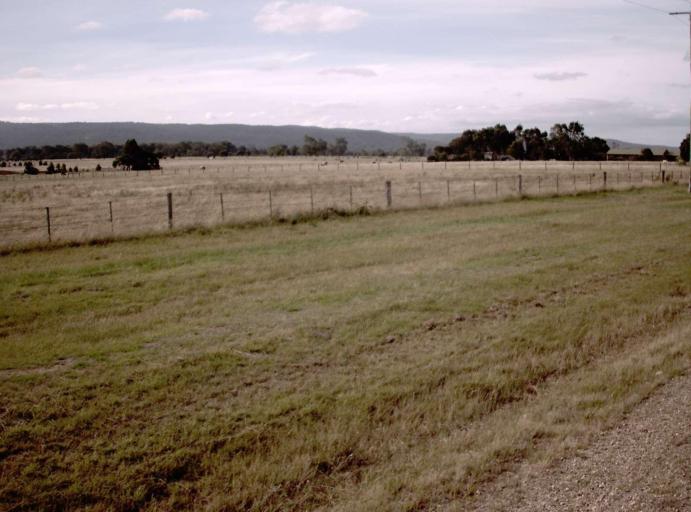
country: AU
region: Victoria
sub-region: Wellington
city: Heyfield
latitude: -38.0420
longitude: 146.6655
